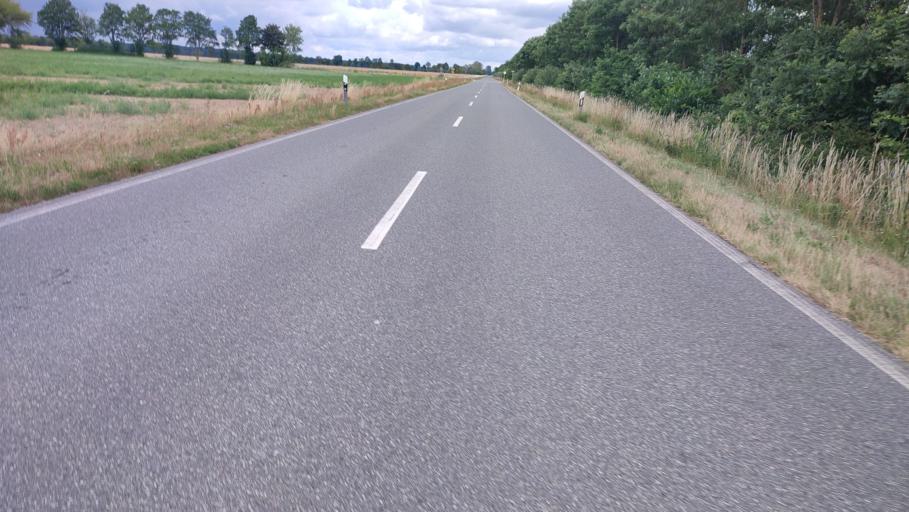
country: DE
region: Lower Saxony
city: Hitzacker
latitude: 53.1963
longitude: 11.1069
